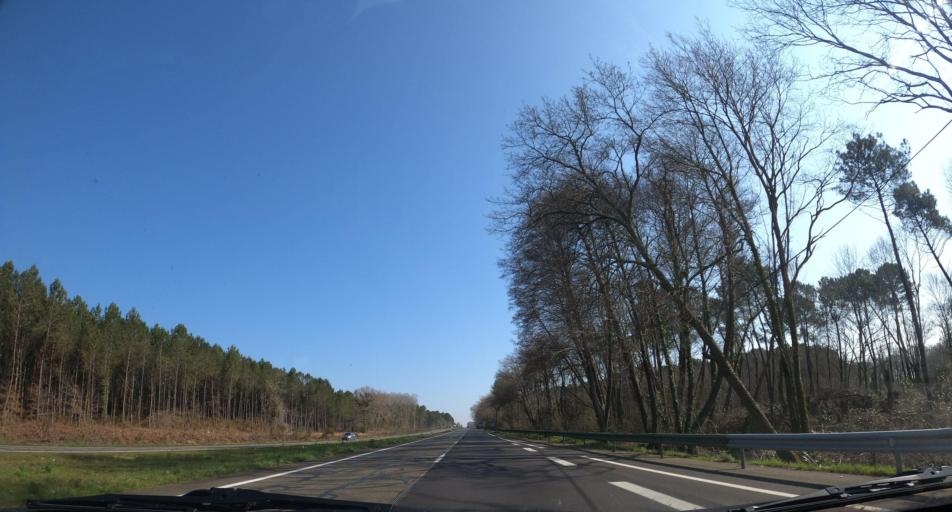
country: FR
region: Aquitaine
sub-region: Departement des Landes
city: Riviere-Saas-et-Gourby
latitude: 43.7007
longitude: -1.1867
